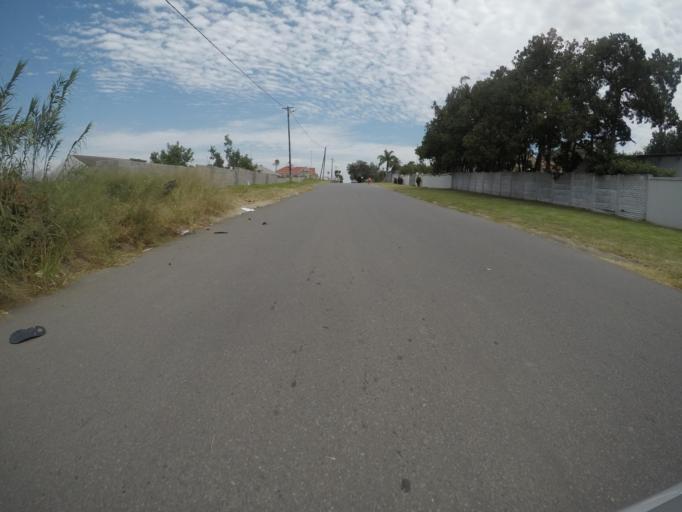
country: ZA
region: Eastern Cape
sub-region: Buffalo City Metropolitan Municipality
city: East London
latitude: -32.9846
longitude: 27.8619
